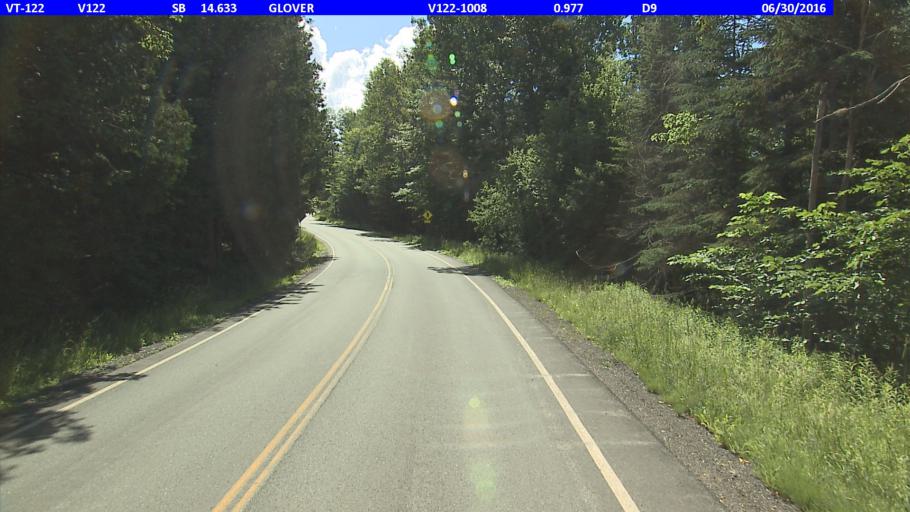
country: US
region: Vermont
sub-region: Caledonia County
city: Lyndonville
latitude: 44.6851
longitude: -72.1813
